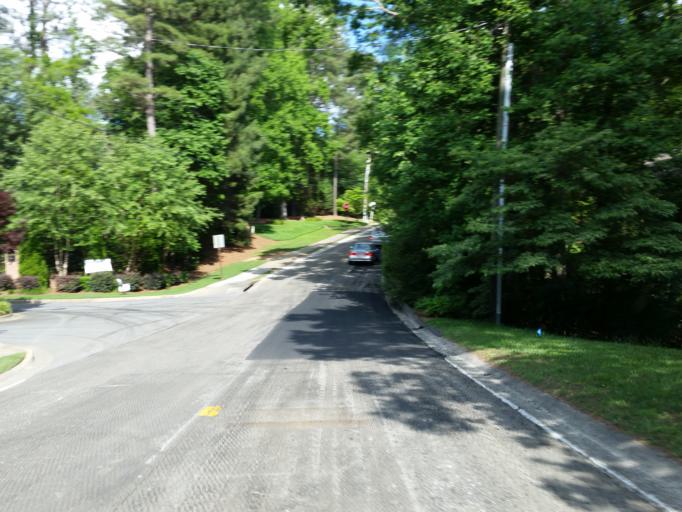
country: US
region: Georgia
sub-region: Fulton County
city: Roswell
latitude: 34.0041
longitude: -84.4219
